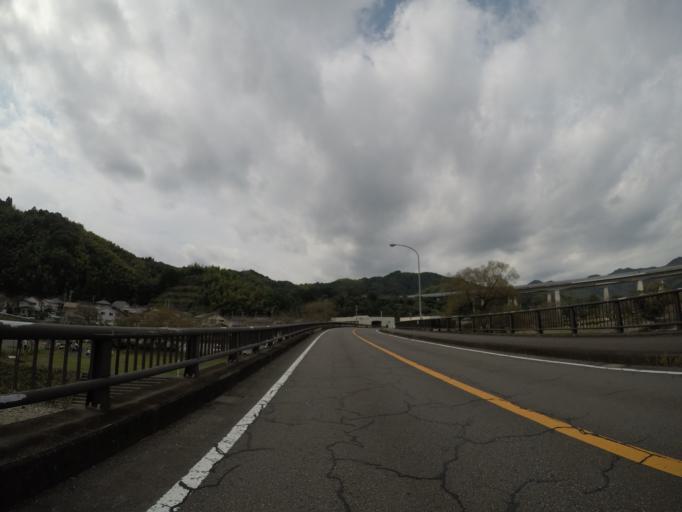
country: JP
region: Shizuoka
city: Fujieda
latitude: 34.8828
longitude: 138.2153
